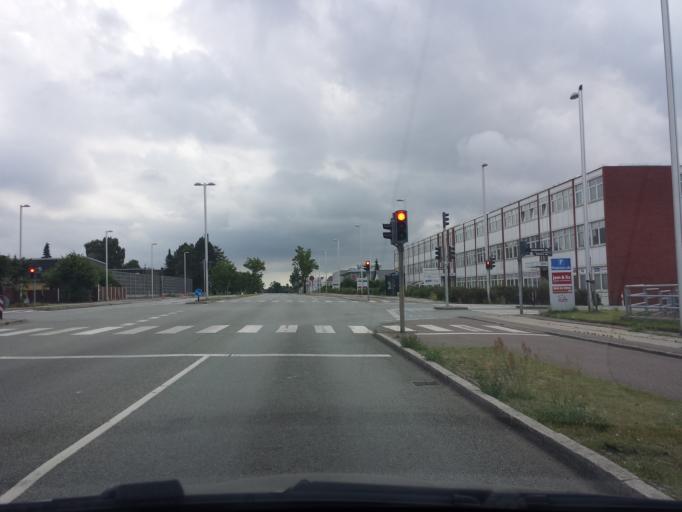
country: DK
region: Capital Region
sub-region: Herlev Kommune
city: Herlev
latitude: 55.7254
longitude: 12.4206
